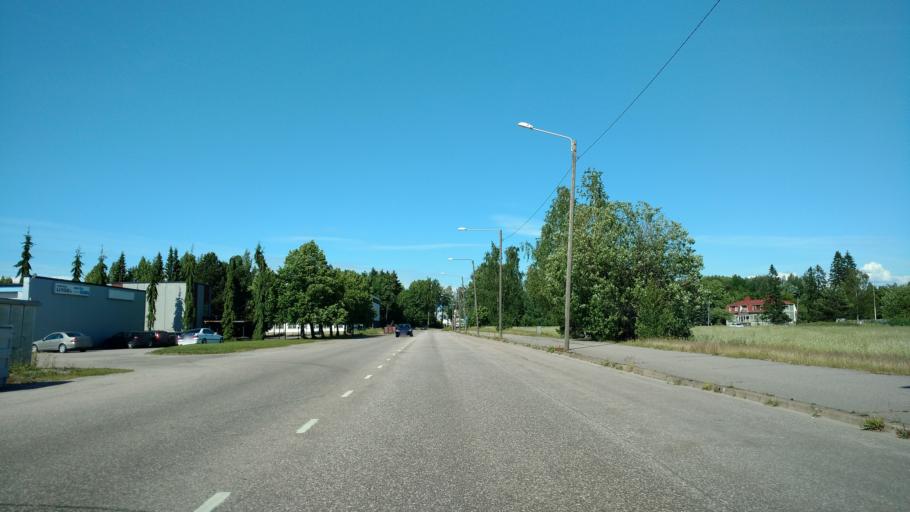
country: FI
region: Varsinais-Suomi
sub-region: Salo
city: Salo
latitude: 60.3773
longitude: 23.1178
